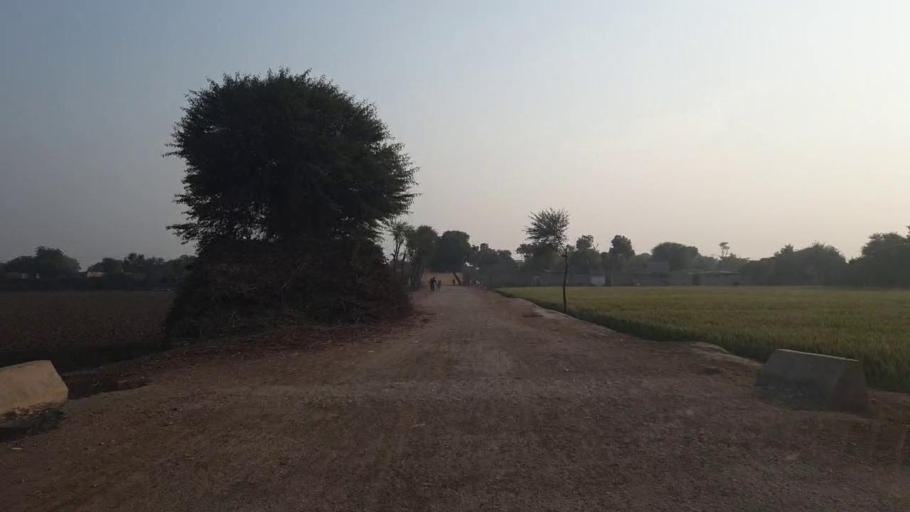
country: PK
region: Sindh
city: Bhit Shah
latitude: 25.8029
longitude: 68.4629
